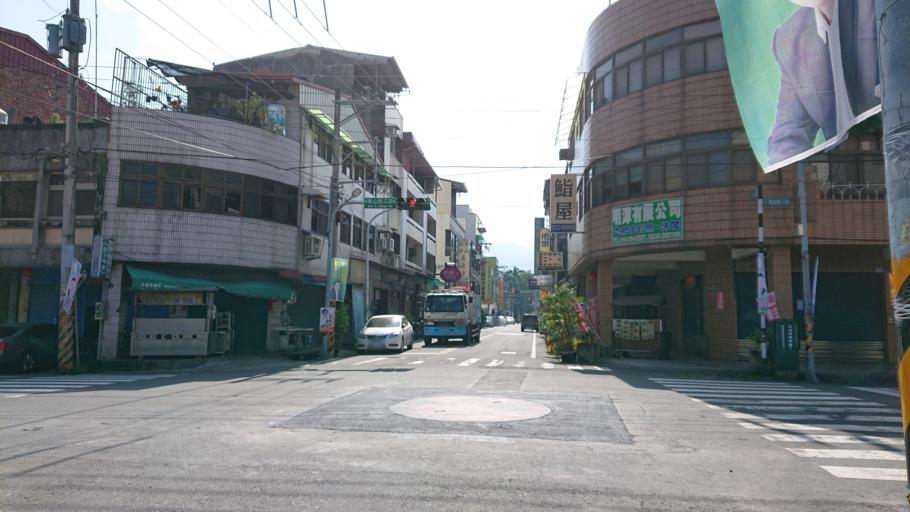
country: TW
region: Taiwan
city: Lugu
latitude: 23.7544
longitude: 120.6798
